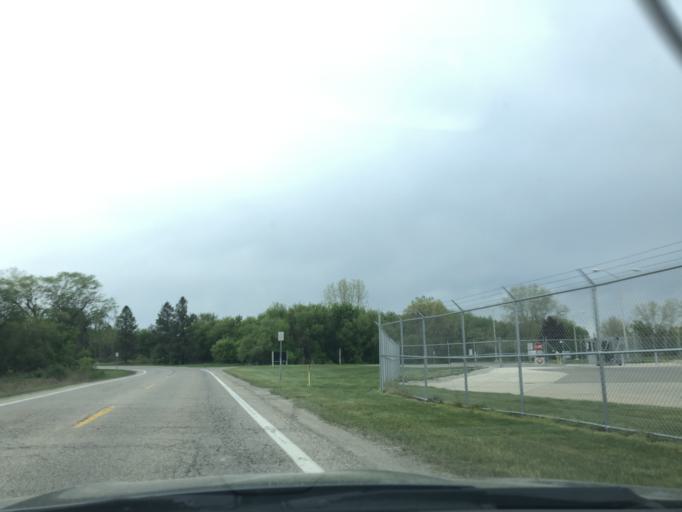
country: US
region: Michigan
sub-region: Eaton County
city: Dimondale
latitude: 42.6674
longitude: -84.6749
